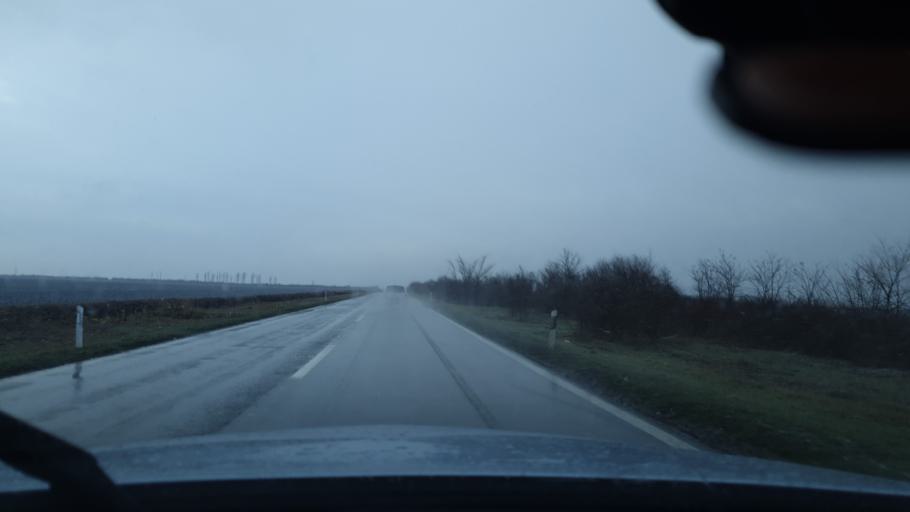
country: RS
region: Autonomna Pokrajina Vojvodina
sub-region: Juznobanatski Okrug
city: Pancevo
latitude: 44.8534
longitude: 20.7634
